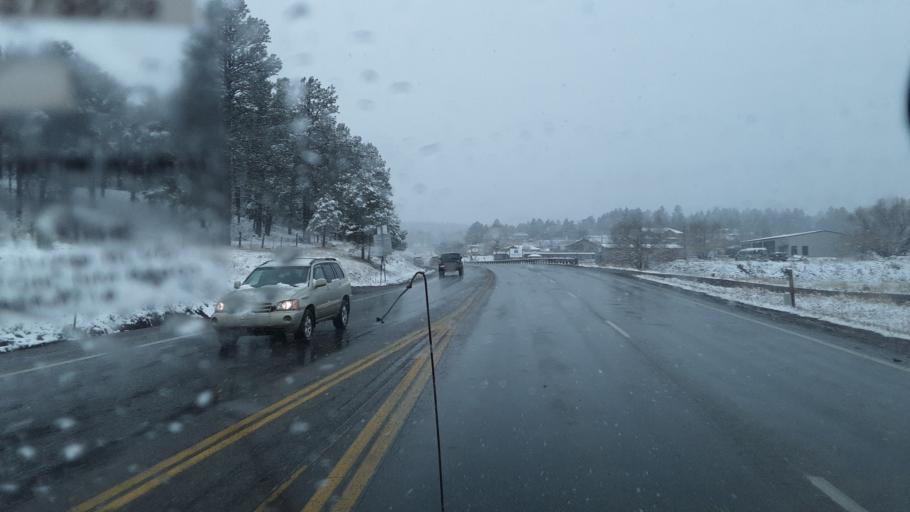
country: US
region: Colorado
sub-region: Archuleta County
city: Pagosa Springs
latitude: 37.2671
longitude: -107.0210
